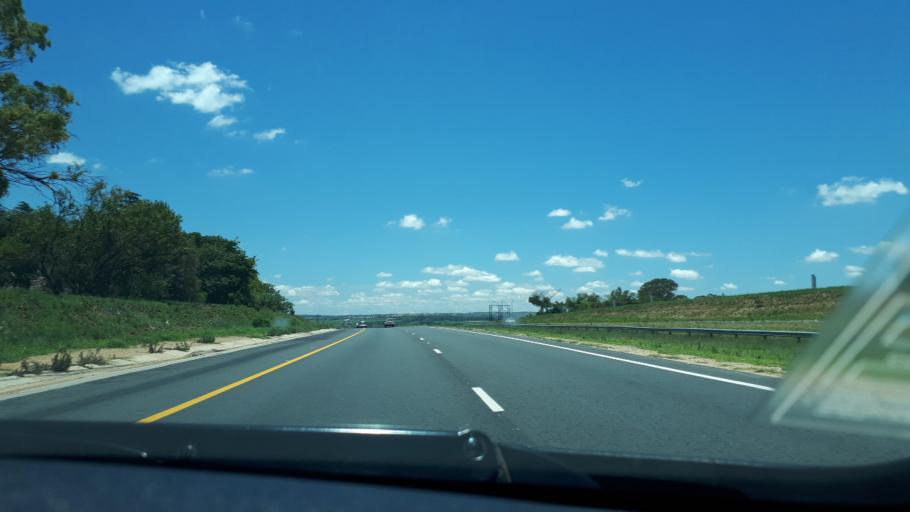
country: ZA
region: Gauteng
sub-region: City of Johannesburg Metropolitan Municipality
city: Diepsloot
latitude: -25.9707
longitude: 27.9436
